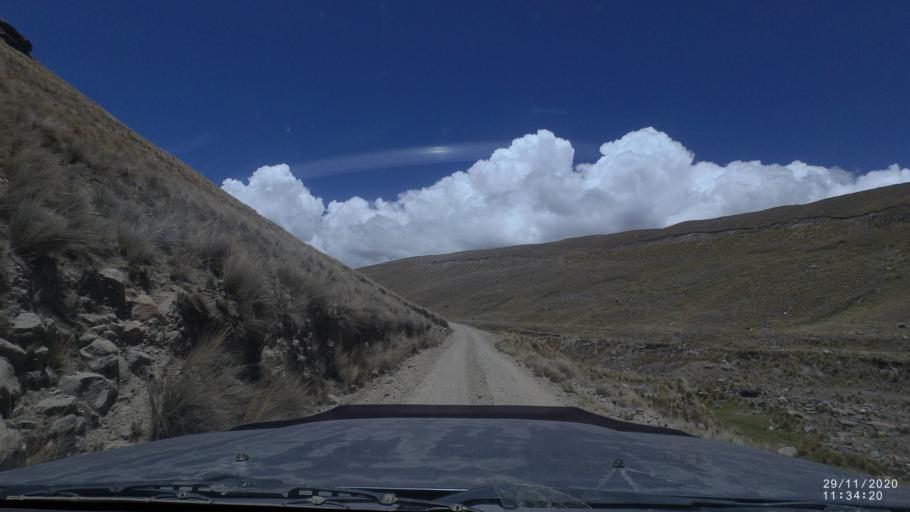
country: BO
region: Cochabamba
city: Cochabamba
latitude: -17.1877
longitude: -66.2198
